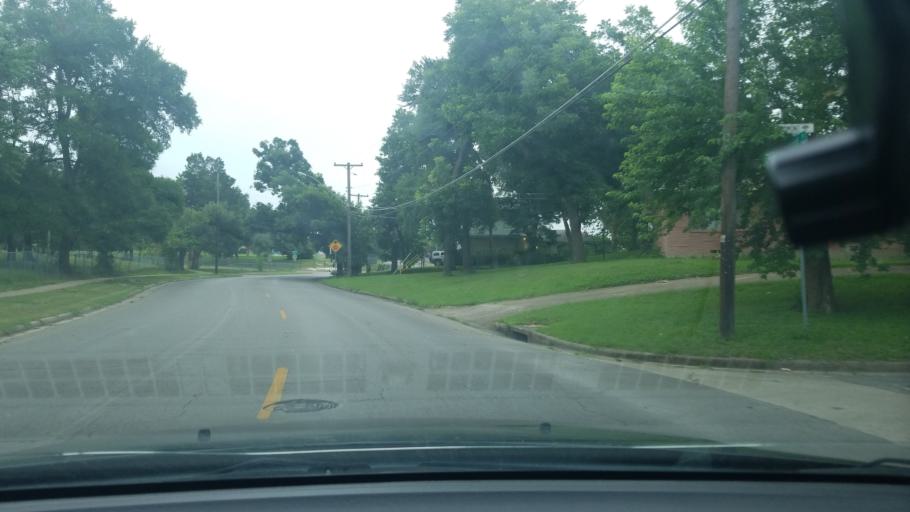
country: US
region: Texas
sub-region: Dallas County
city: Balch Springs
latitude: 32.7603
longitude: -96.6880
